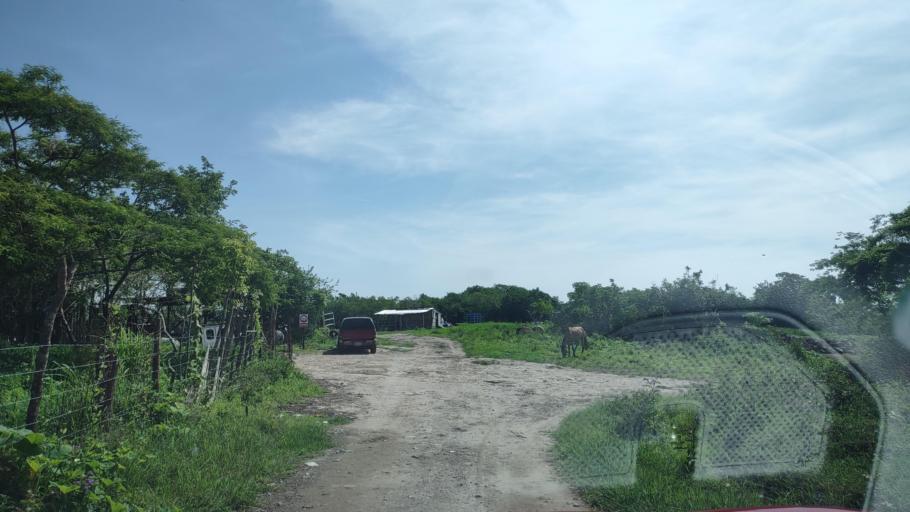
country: MX
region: Veracruz
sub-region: Emiliano Zapata
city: Dos Rios
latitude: 19.4301
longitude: -96.7996
